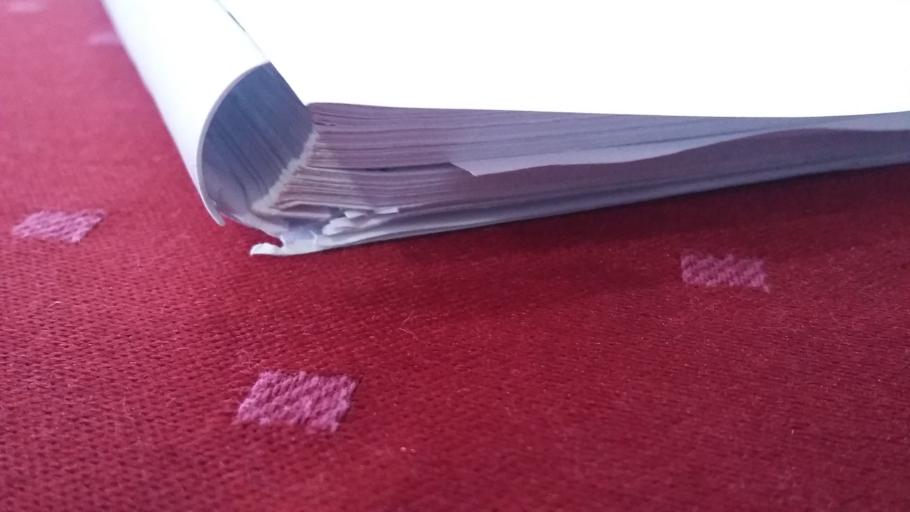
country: MZ
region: Nampula
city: Nampula
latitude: -15.1141
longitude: 39.2576
